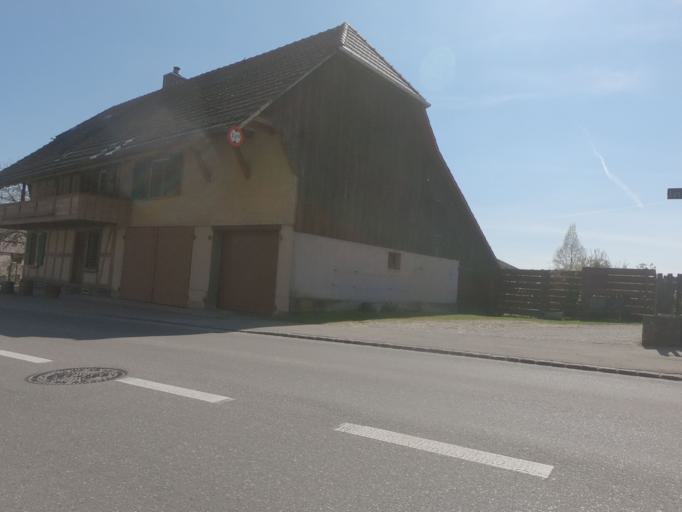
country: CH
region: Bern
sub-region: Biel/Bienne District
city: Orpund
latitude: 47.1200
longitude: 7.3422
